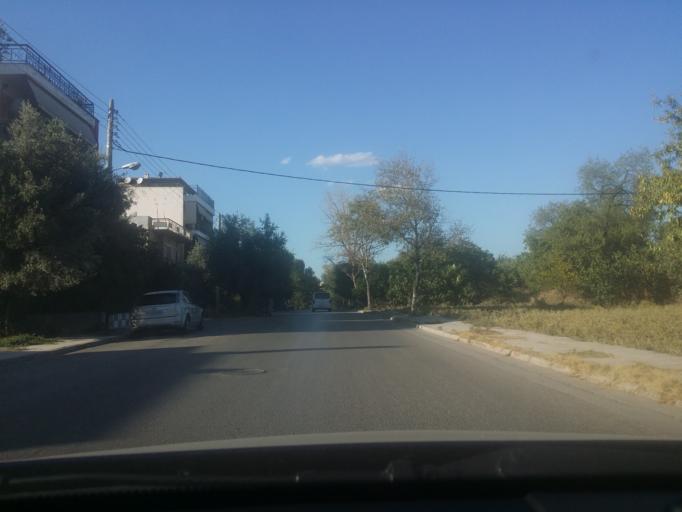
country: GR
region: Attica
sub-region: Nomarchia Athinas
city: Cholargos
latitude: 38.0116
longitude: 23.8023
